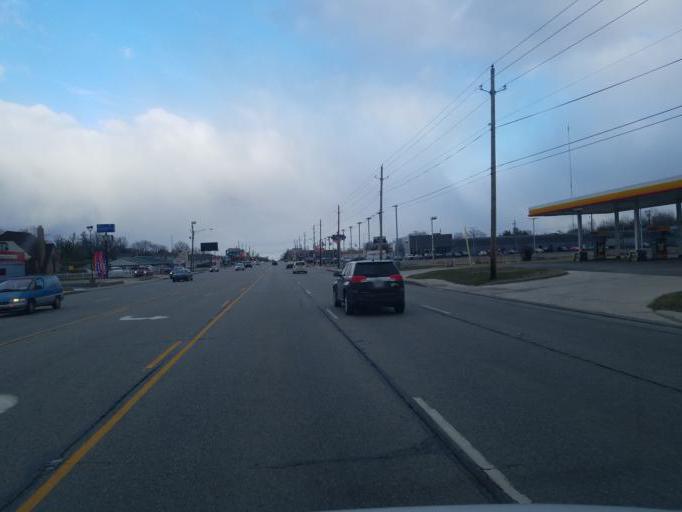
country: US
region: Indiana
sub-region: Marion County
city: Warren Park
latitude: 39.7735
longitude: -86.0180
